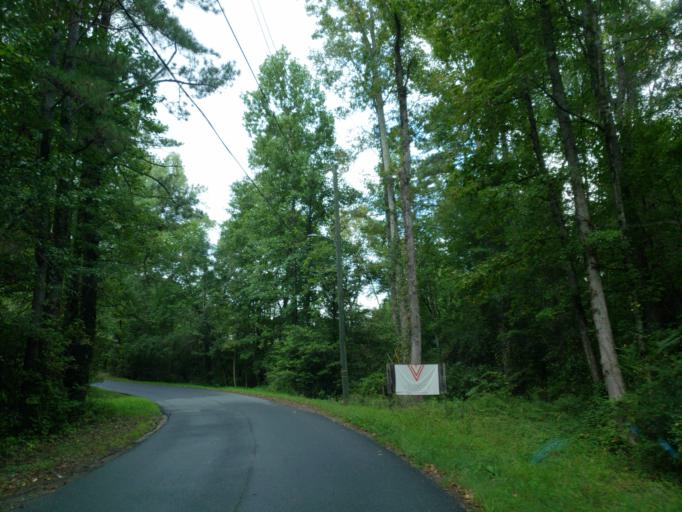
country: US
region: Georgia
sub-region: Cherokee County
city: Holly Springs
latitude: 34.1605
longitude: -84.5092
